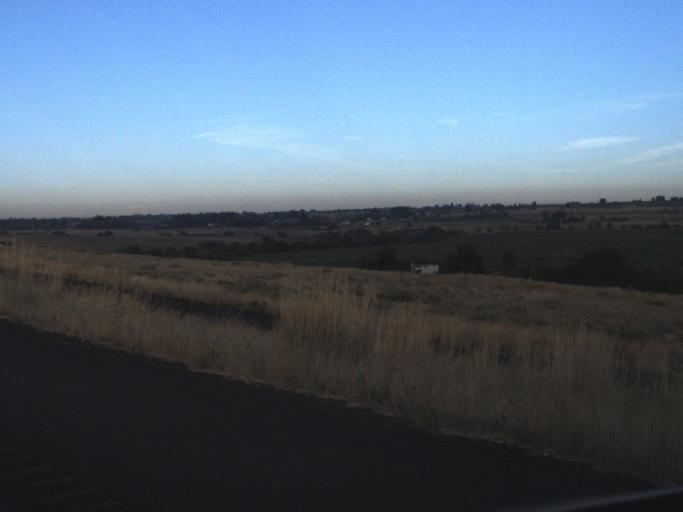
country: US
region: Washington
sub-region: Benton County
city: Prosser
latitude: 46.2401
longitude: -119.6431
